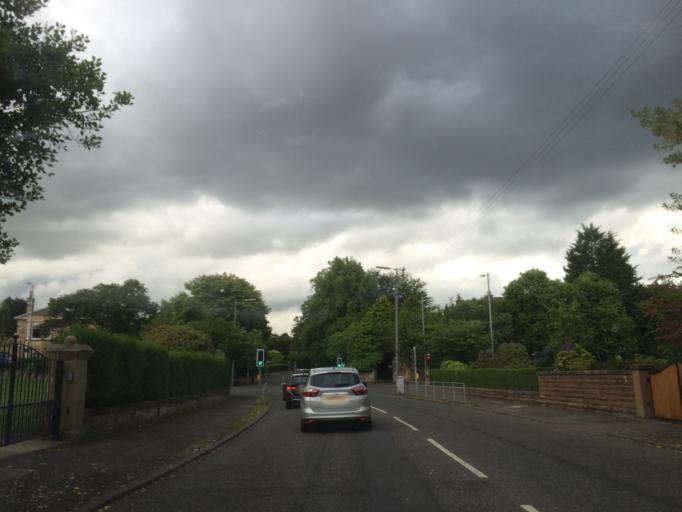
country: GB
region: Scotland
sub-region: East Renfrewshire
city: Giffnock
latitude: 55.8147
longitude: -4.2781
